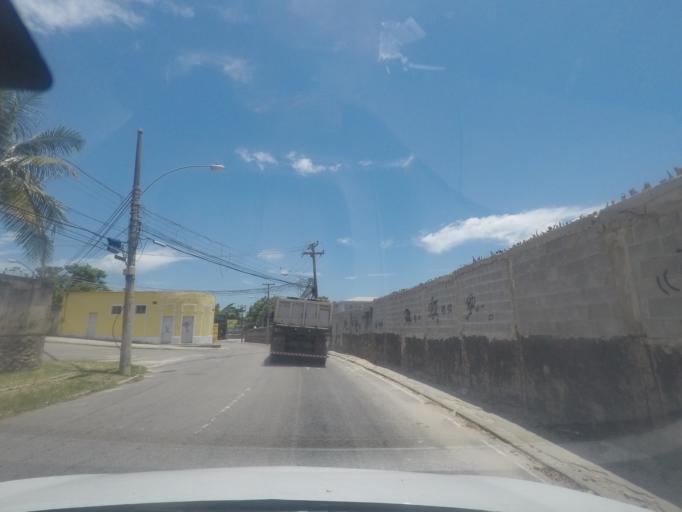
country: BR
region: Rio de Janeiro
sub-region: Itaguai
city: Itaguai
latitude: -22.9218
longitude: -43.6919
